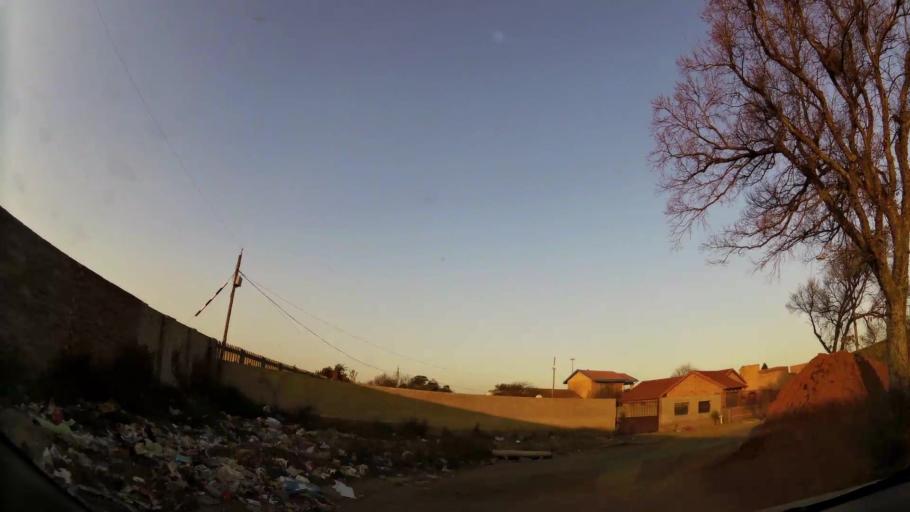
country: ZA
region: Gauteng
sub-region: West Rand District Municipality
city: Randfontein
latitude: -26.2014
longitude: 27.7060
